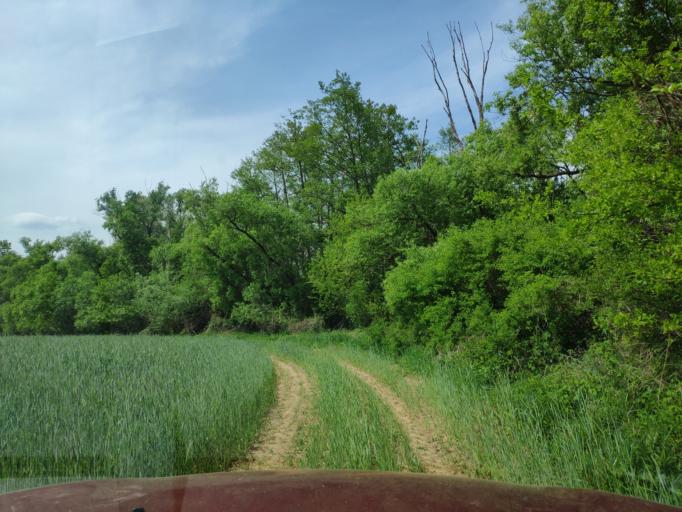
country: SK
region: Banskobystricky
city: Rimavska Sobota
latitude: 48.4786
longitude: 20.0794
